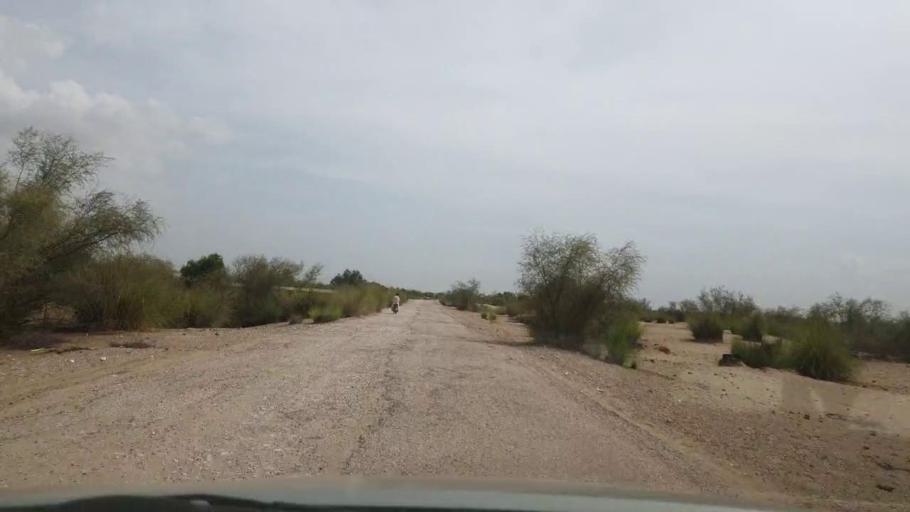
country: PK
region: Sindh
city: Bozdar
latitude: 27.0985
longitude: 69.0179
